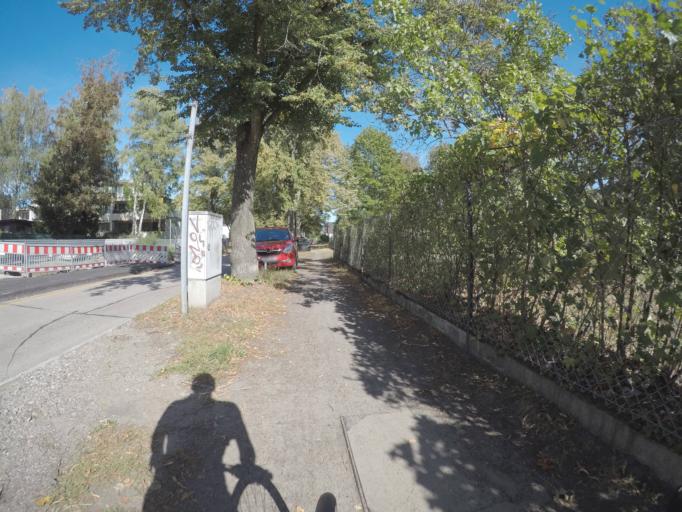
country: DE
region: Berlin
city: Heiligensee
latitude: 52.6146
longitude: 13.2191
